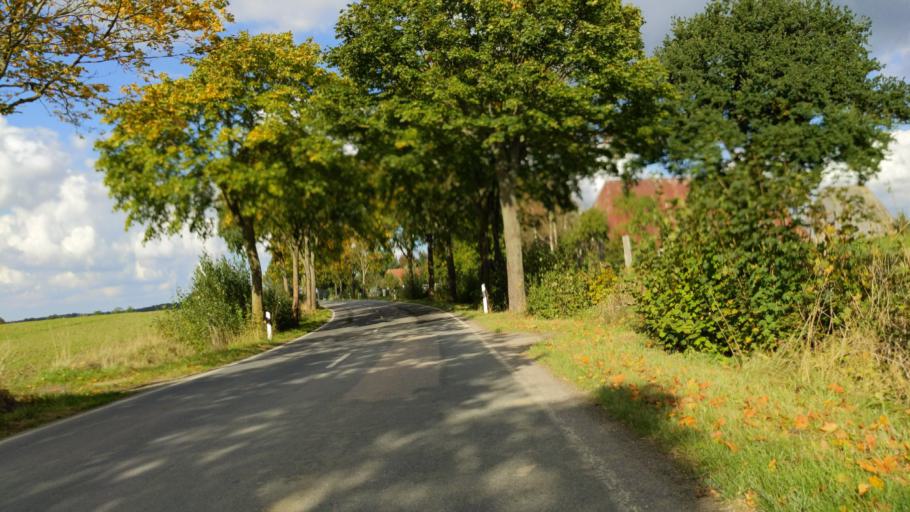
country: DE
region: Schleswig-Holstein
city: Ahrensbok
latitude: 54.0135
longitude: 10.5853
